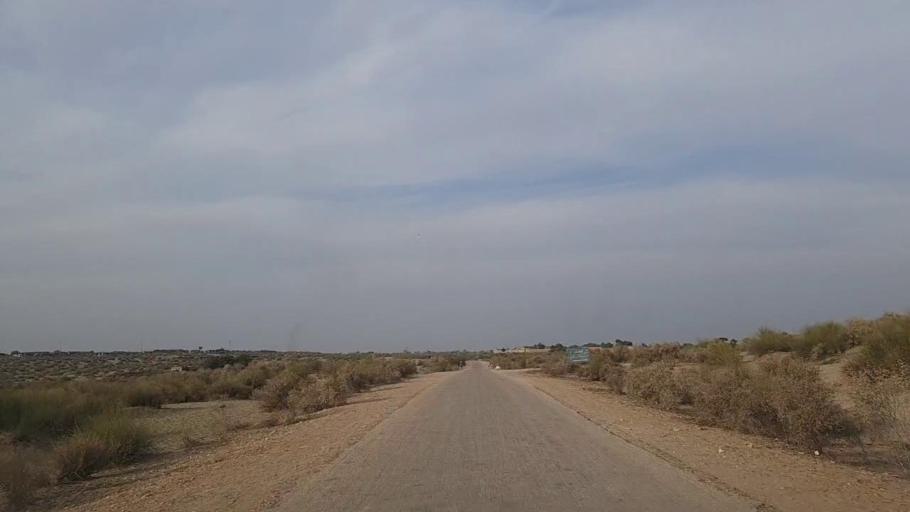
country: PK
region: Sindh
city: Daur
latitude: 26.5062
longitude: 68.4410
